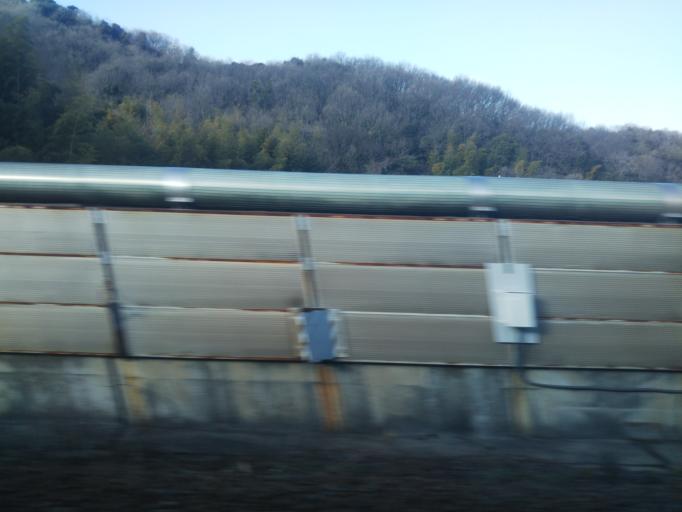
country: JP
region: Kagawa
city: Sakaidecho
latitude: 34.4498
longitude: 133.8077
